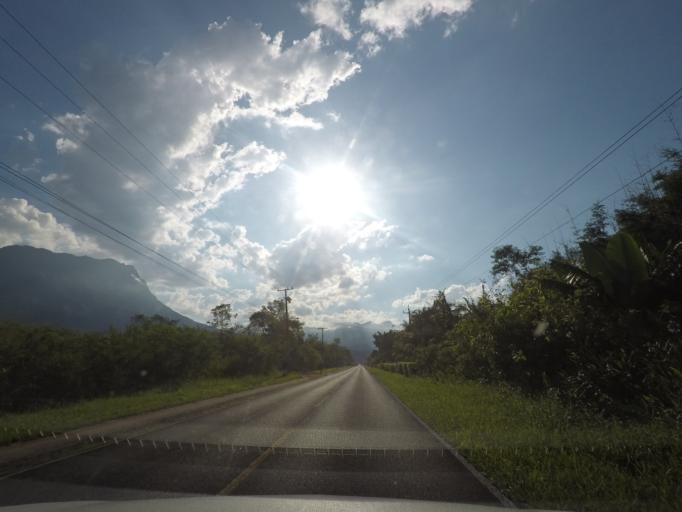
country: BR
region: Parana
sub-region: Antonina
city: Antonina
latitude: -25.4544
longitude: -48.8622
